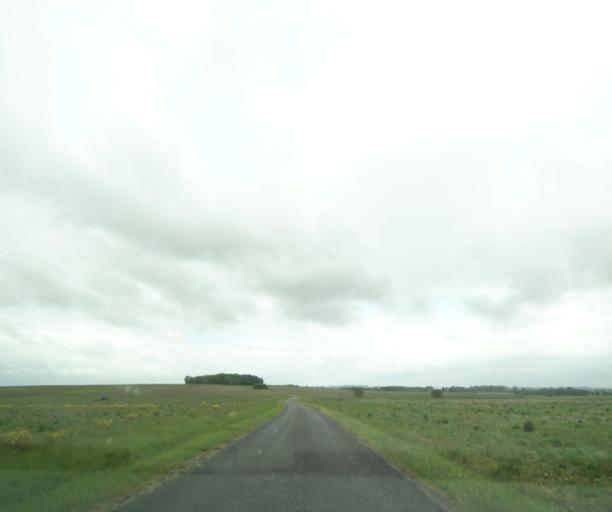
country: FR
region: Poitou-Charentes
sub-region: Departement de la Charente-Maritime
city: Perignac
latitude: 45.6685
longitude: -0.4978
